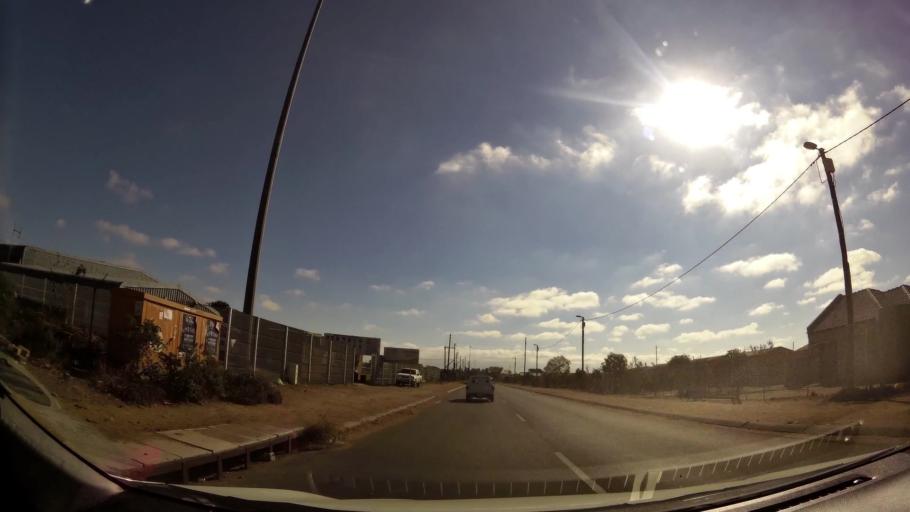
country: ZA
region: Limpopo
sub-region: Capricorn District Municipality
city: Polokwane
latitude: -23.8494
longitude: 29.3996
